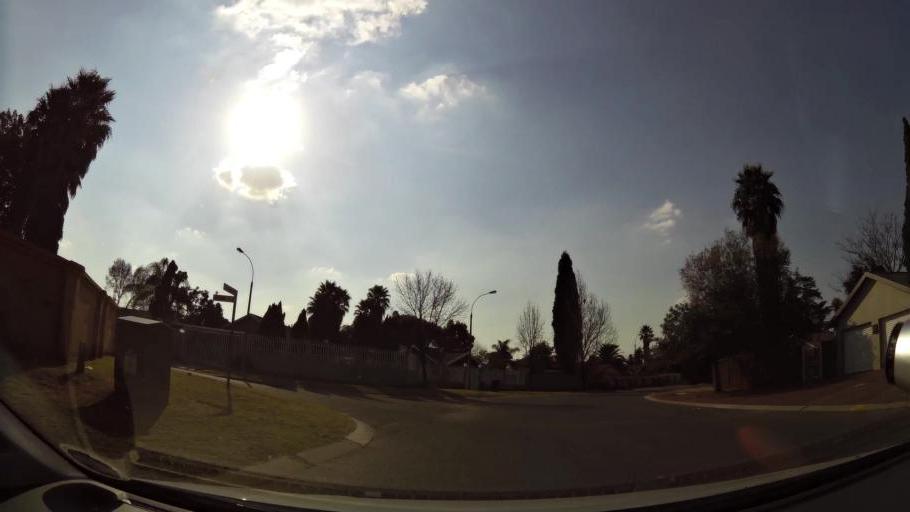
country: ZA
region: Gauteng
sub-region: City of Johannesburg Metropolitan Municipality
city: Modderfontein
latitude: -26.0819
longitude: 28.1924
